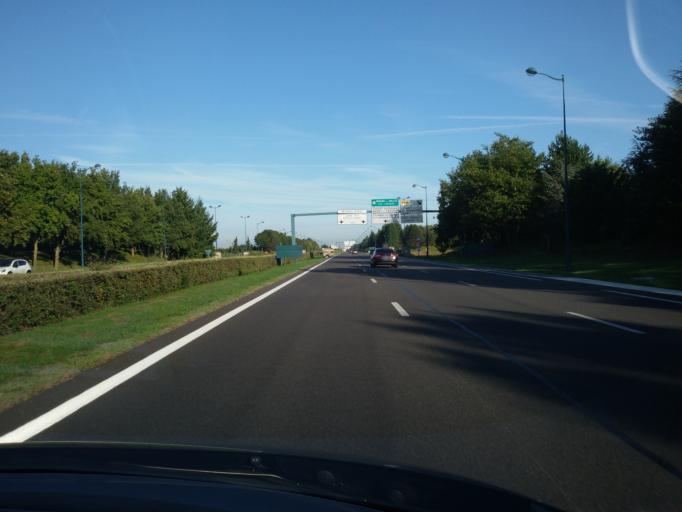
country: FR
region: Ile-de-France
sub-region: Departement de Seine-et-Marne
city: Bailly-Romainvilliers
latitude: 48.8466
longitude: 2.8108
